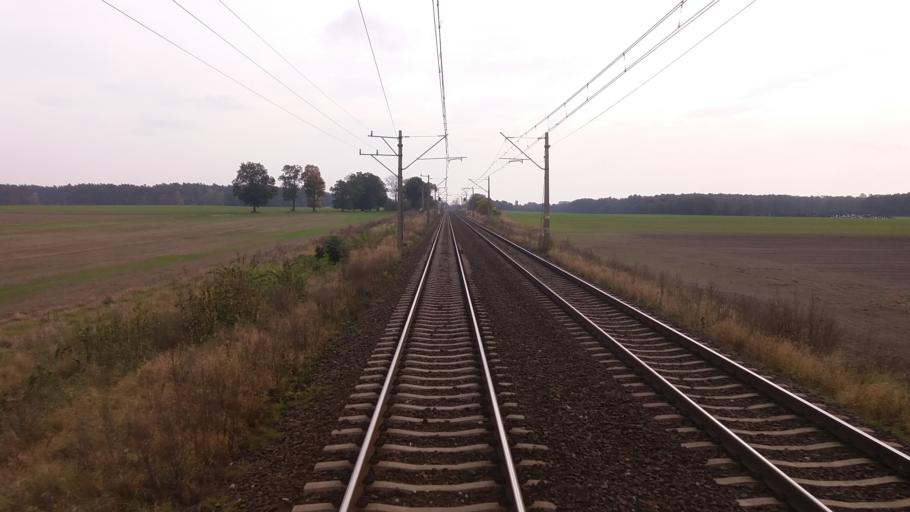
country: PL
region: West Pomeranian Voivodeship
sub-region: Powiat stargardzki
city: Dolice
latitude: 53.2161
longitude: 15.1590
